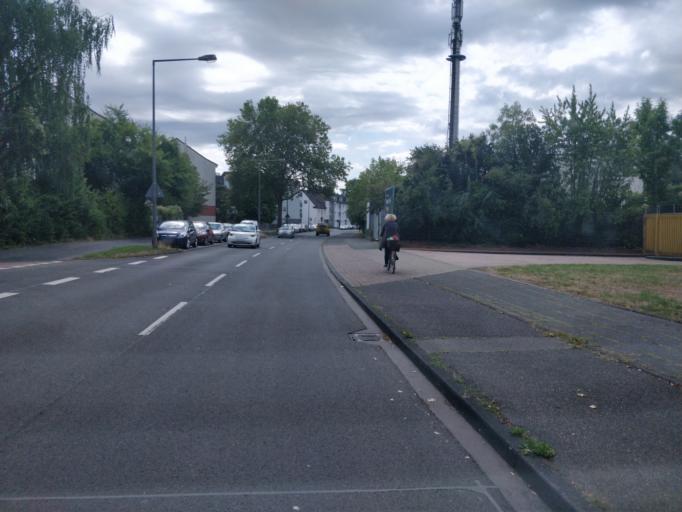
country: DE
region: North Rhine-Westphalia
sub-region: Regierungsbezirk Koln
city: Neuehrenfeld
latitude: 50.9636
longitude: 6.9353
